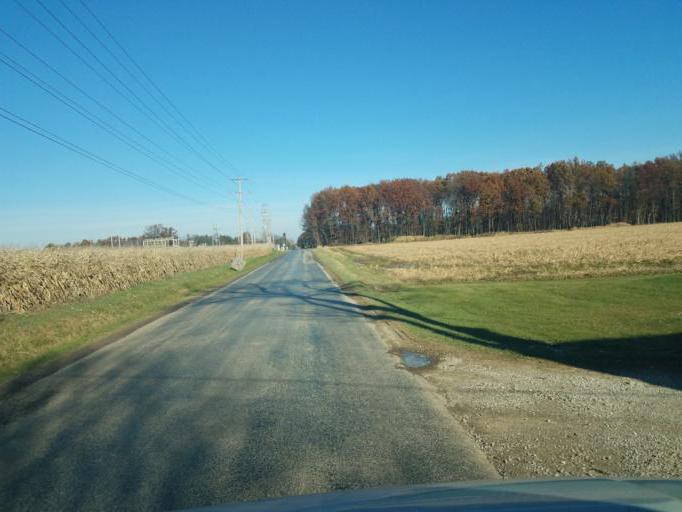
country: US
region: Ohio
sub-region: Ashland County
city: Ashland
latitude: 40.8197
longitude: -82.3494
